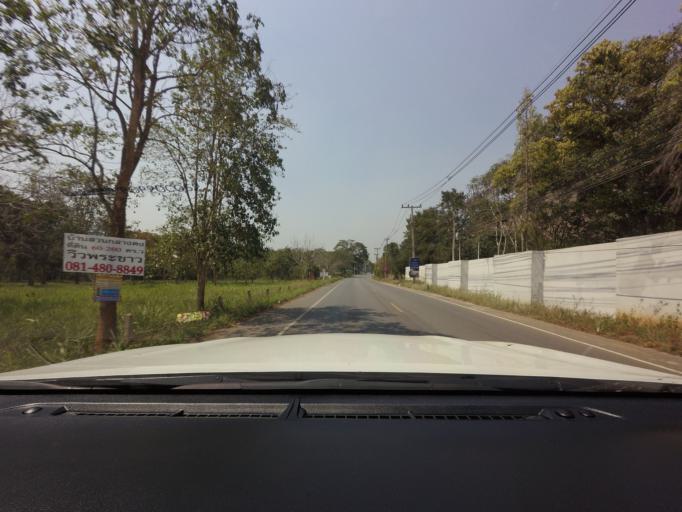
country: TH
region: Sara Buri
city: Muak Lek
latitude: 14.5449
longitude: 101.3315
